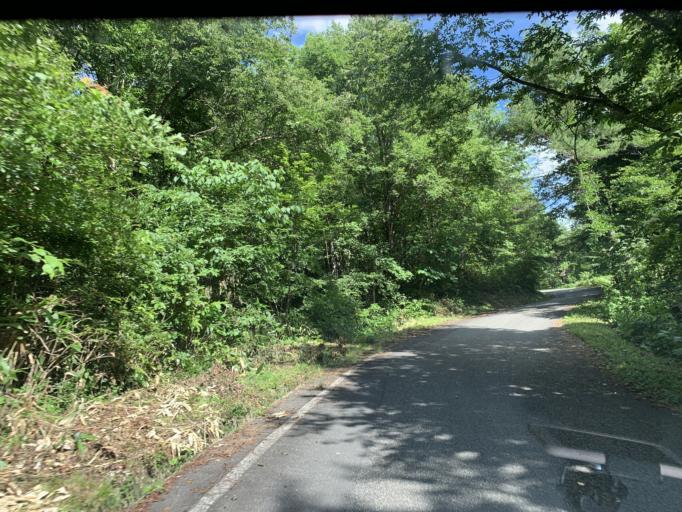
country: JP
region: Iwate
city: Ichinoseki
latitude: 38.9269
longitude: 140.9290
